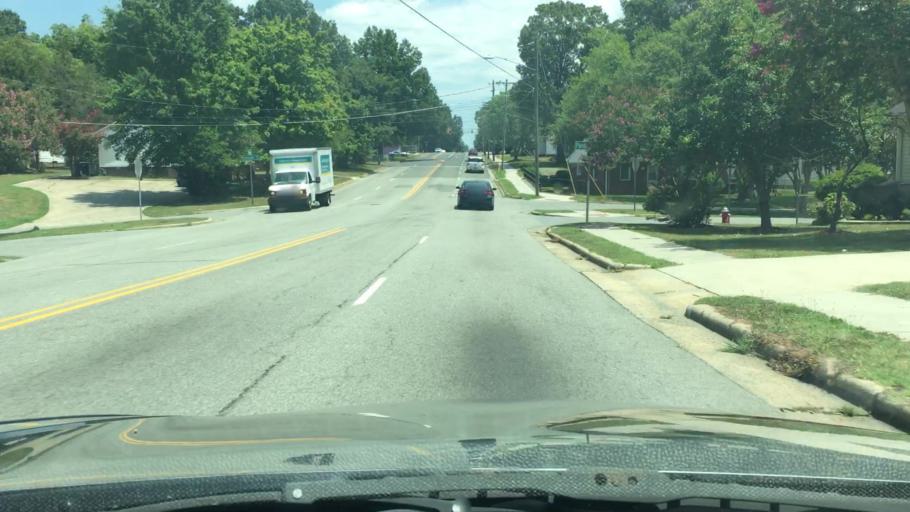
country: US
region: North Carolina
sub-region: Alamance County
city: Burlington
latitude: 36.0933
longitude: -79.4164
